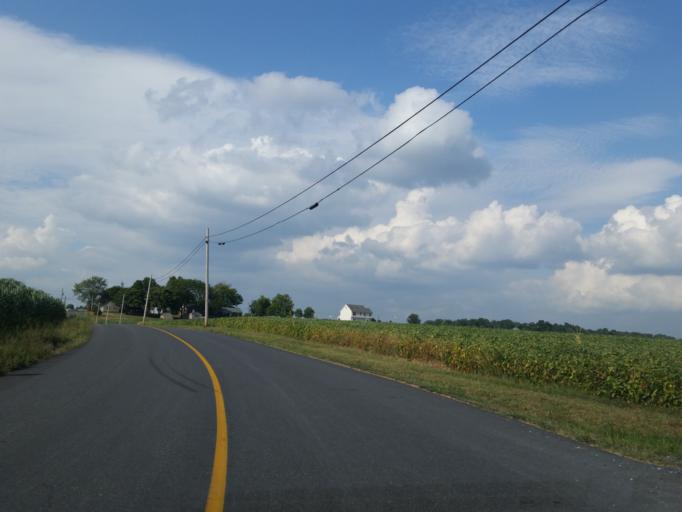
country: US
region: Pennsylvania
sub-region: Lancaster County
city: Manheim
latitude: 40.1607
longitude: -76.4564
